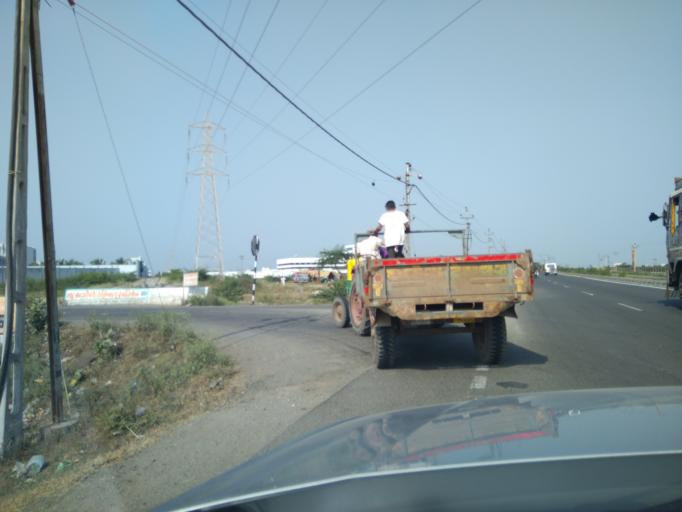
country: IN
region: Gujarat
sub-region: Jamnagar
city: Jamnagar
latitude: 22.4225
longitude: 70.0508
